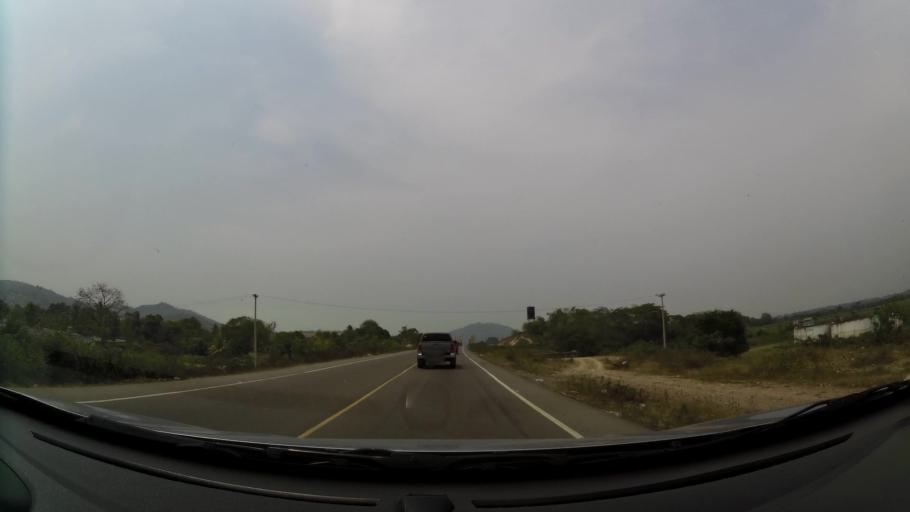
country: HN
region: Cortes
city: Potrerillos
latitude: 15.2341
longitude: -87.9587
